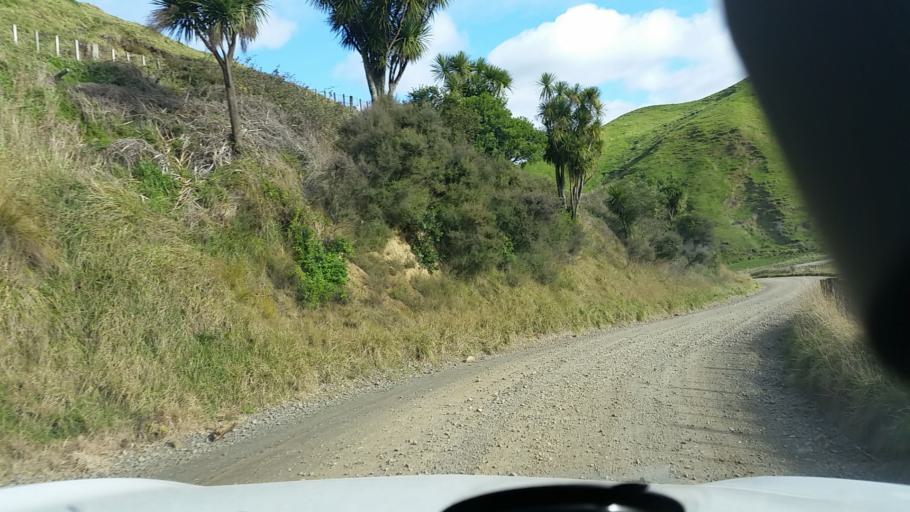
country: NZ
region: Hawke's Bay
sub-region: Napier City
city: Napier
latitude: -39.1113
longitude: 176.8950
